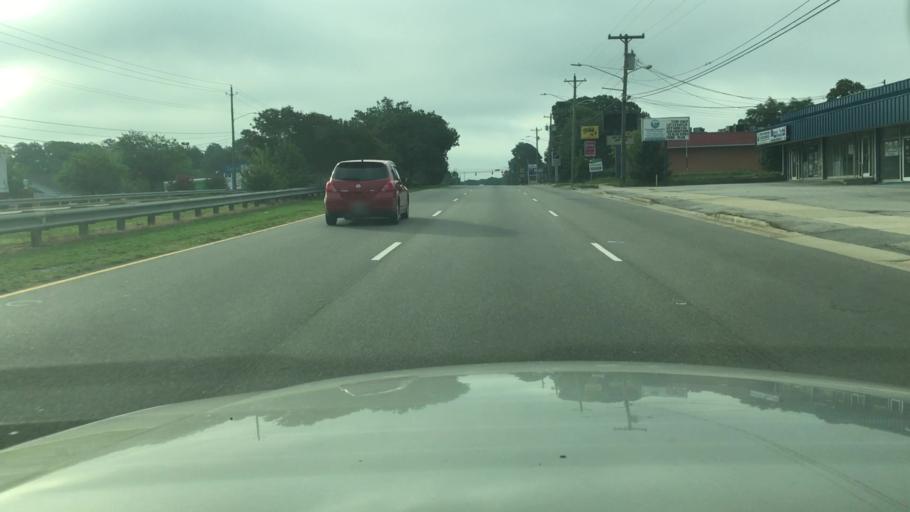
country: US
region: North Carolina
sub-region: Cumberland County
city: Fayetteville
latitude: 35.0732
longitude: -78.9258
